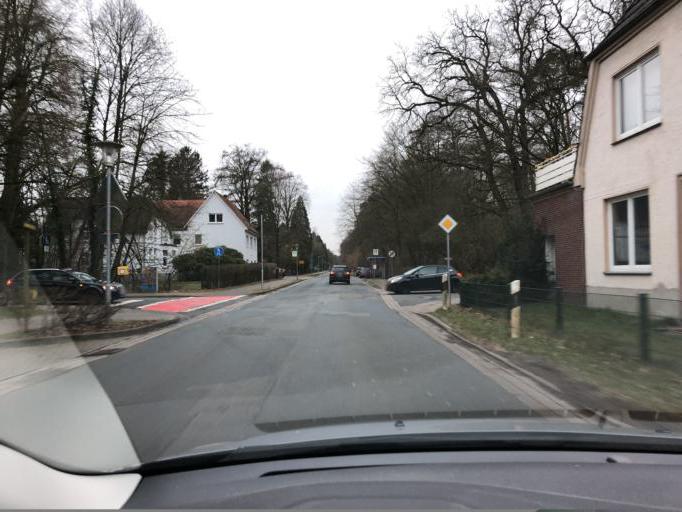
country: DE
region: Lower Saxony
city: Delmenhorst
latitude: 53.0828
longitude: 8.5752
